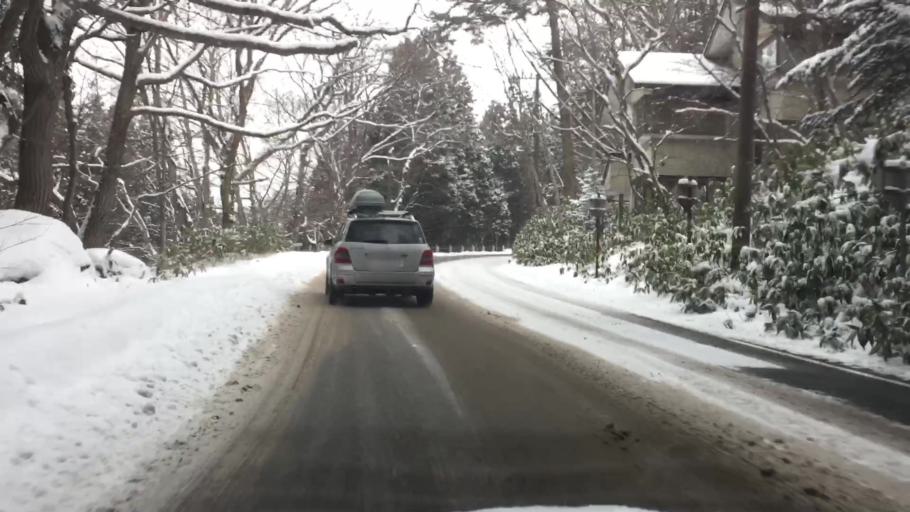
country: JP
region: Tochigi
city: Yaita
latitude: 36.9562
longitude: 139.7784
